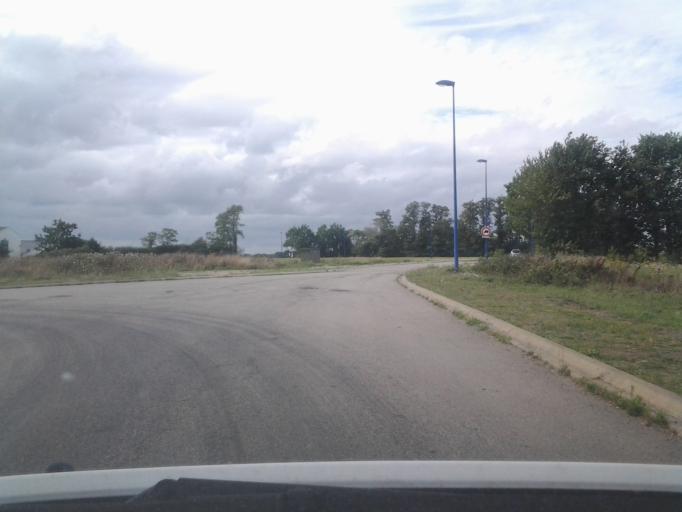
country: FR
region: Pays de la Loire
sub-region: Departement de la Vendee
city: Dompierre-sur-Yon
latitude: 46.6956
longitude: -1.3677
